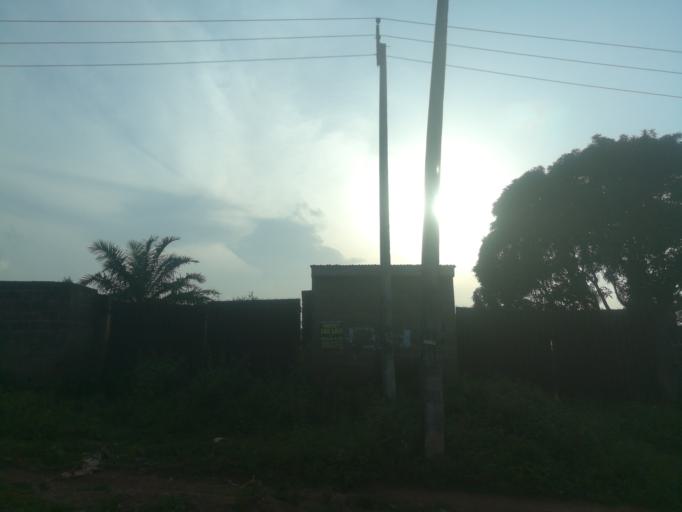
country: NG
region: Oyo
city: Moniya
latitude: 7.5407
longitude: 3.8993
